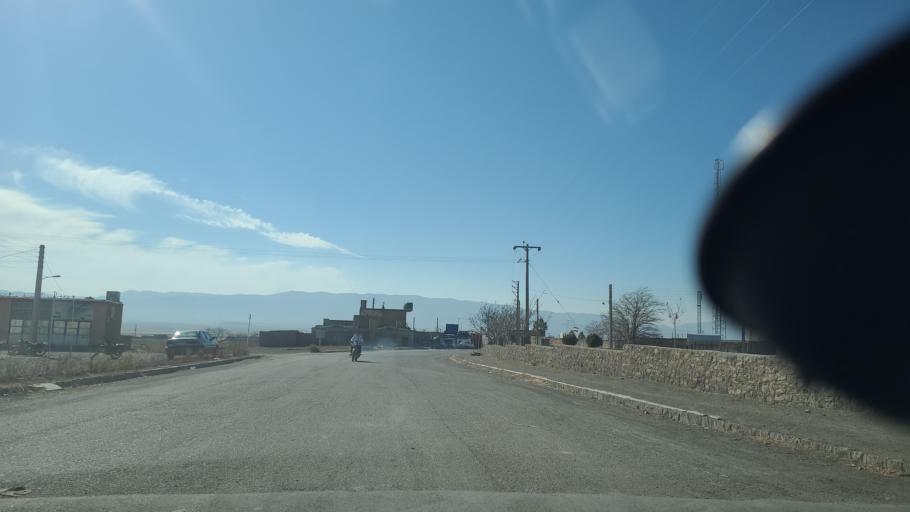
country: IR
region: Razavi Khorasan
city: Dowlatabad
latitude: 35.6216
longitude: 59.4786
